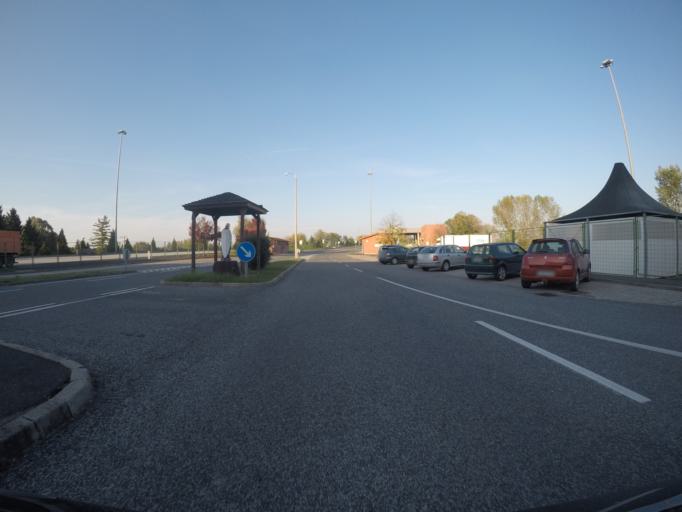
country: HU
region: Somogy
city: Barcs
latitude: 45.9479
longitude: 17.4627
